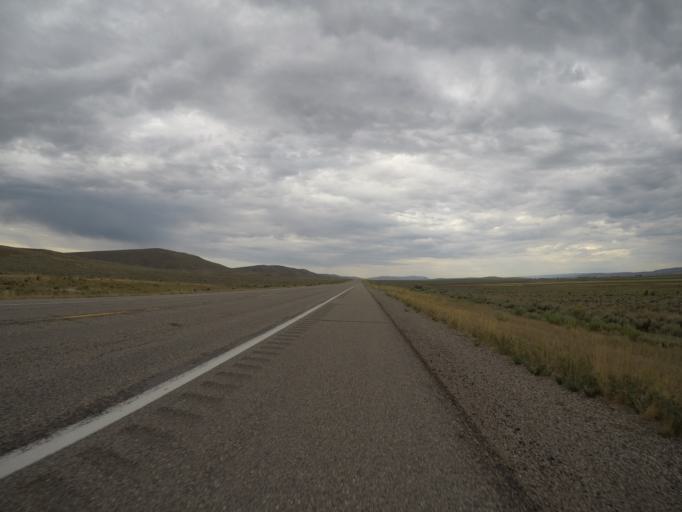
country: US
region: Utah
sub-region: Rich County
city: Randolph
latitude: 41.8962
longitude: -110.9597
